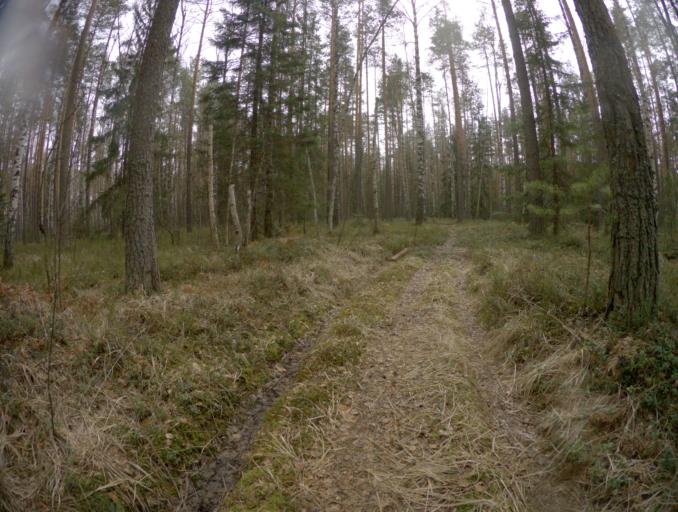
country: RU
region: Vladimir
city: Raduzhnyy
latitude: 55.9502
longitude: 40.2845
